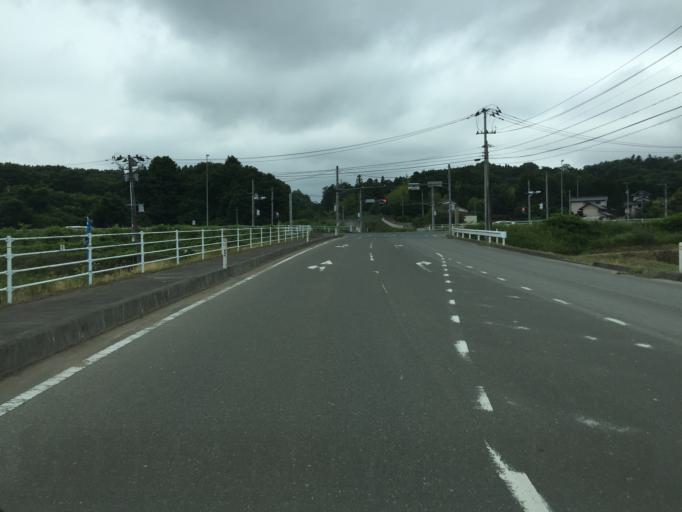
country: JP
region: Fukushima
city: Namie
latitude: 37.7274
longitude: 140.9542
